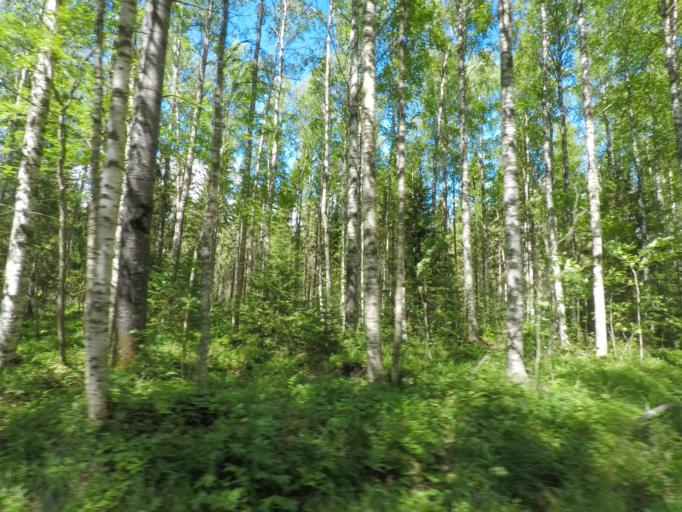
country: FI
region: Central Finland
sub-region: Jyvaeskylae
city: Hankasalmi
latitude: 62.4393
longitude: 26.6480
